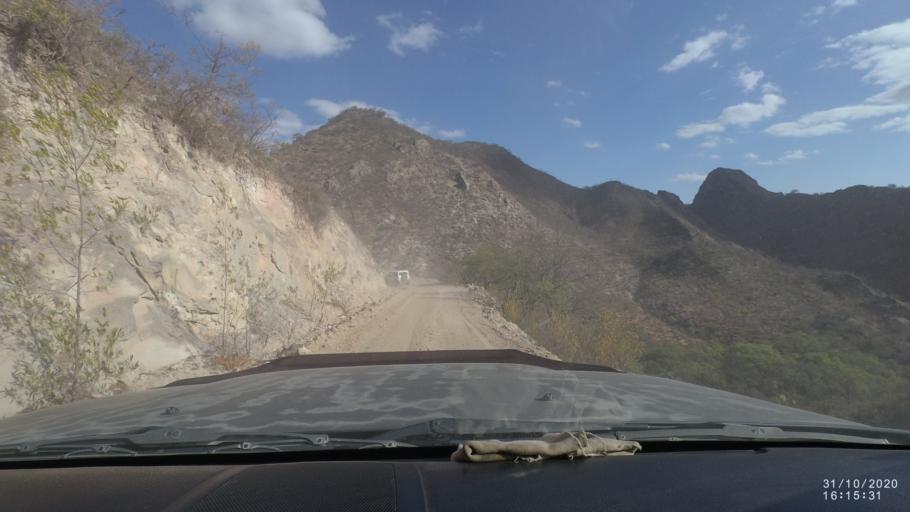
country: BO
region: Chuquisaca
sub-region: Provincia Zudanez
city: Mojocoya
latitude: -18.3887
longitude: -64.6125
